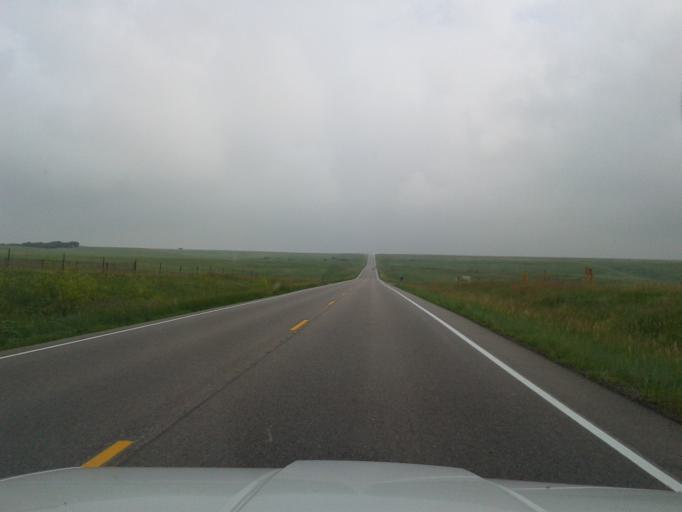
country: US
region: Colorado
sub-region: Elbert County
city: Ponderosa Park
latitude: 39.2939
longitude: -104.7361
